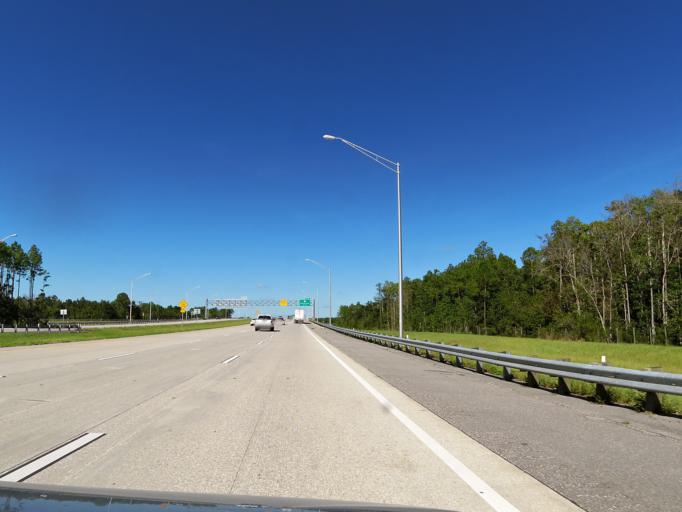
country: US
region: Florida
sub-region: Saint Johns County
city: Palm Valley
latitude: 30.1291
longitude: -81.5105
